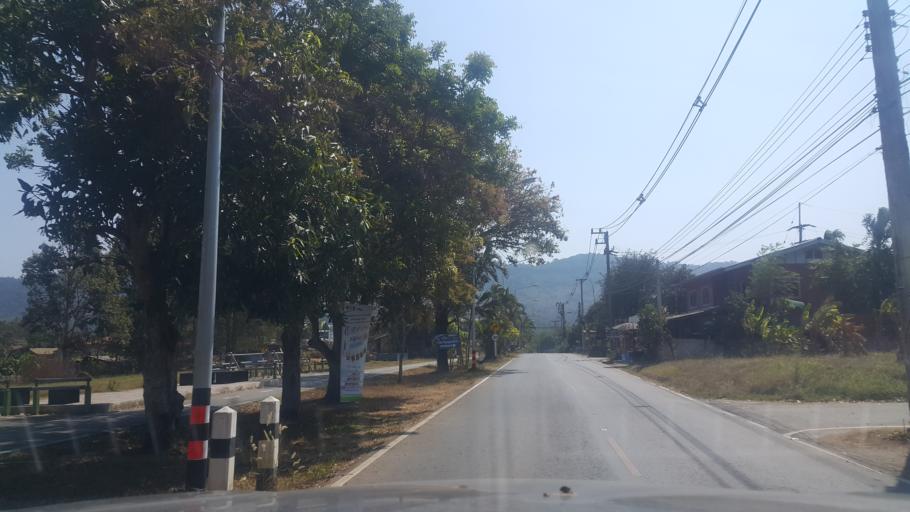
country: TH
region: Nakhon Ratchasima
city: Wang Nam Khiao
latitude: 14.3478
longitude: 101.9400
